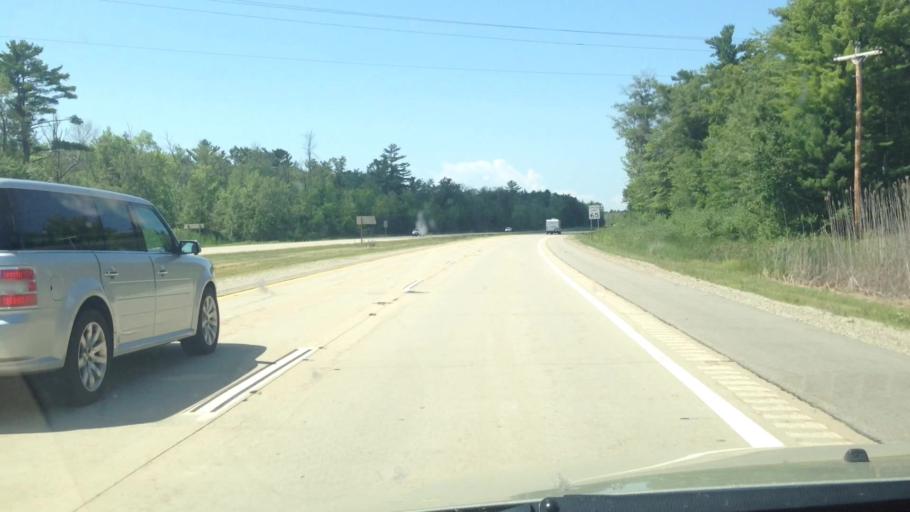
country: US
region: Wisconsin
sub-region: Oconto County
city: Oconto
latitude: 44.8163
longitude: -87.9455
